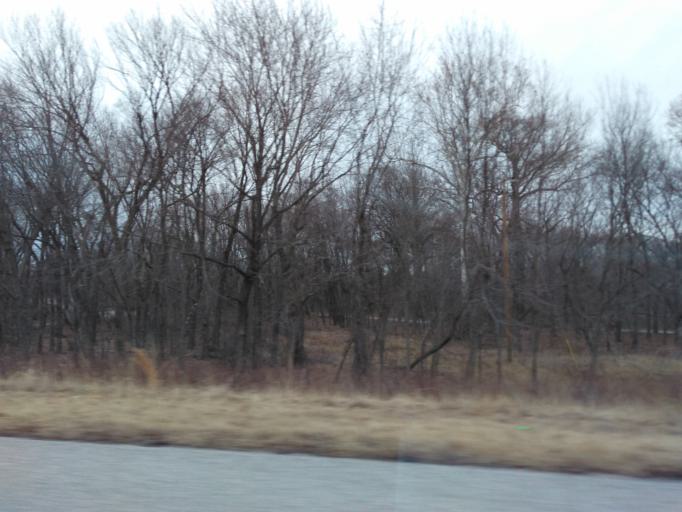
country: US
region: Illinois
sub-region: Clinton County
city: Albers
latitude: 38.4875
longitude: -89.5935
